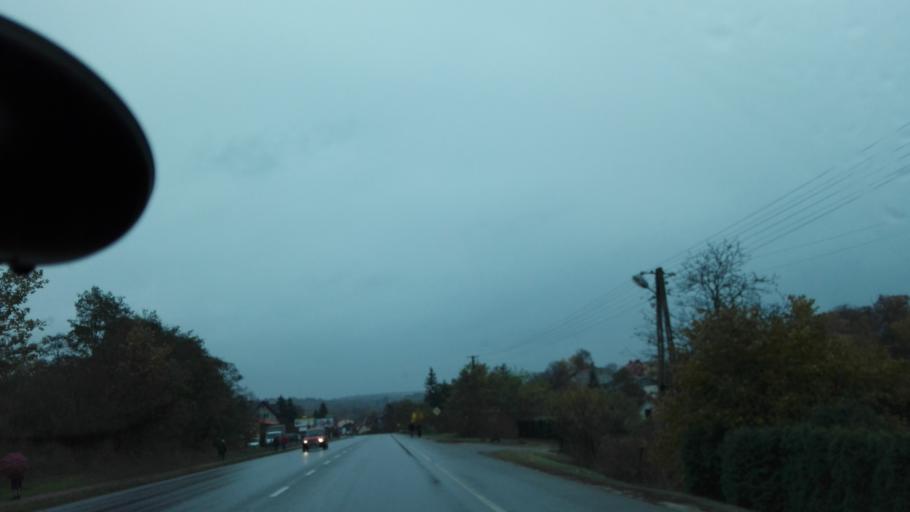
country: PL
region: Lublin Voivodeship
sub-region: Powiat pulawski
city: Pulawy
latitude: 51.4098
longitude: 21.9269
